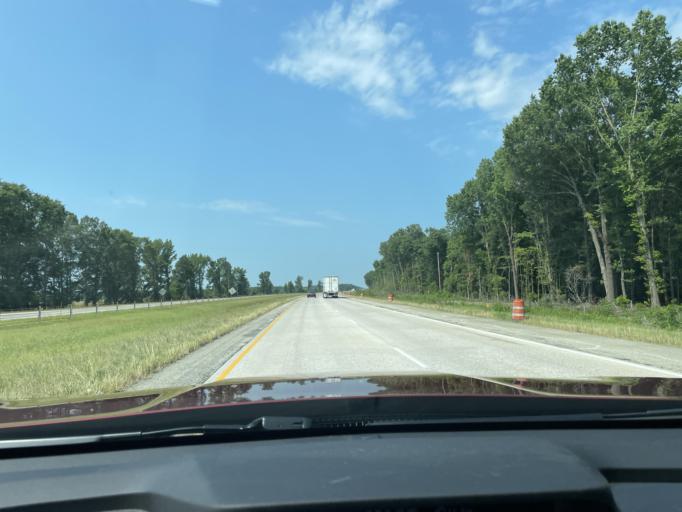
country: US
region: Arkansas
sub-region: White County
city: Searcy
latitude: 35.1531
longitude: -91.7898
